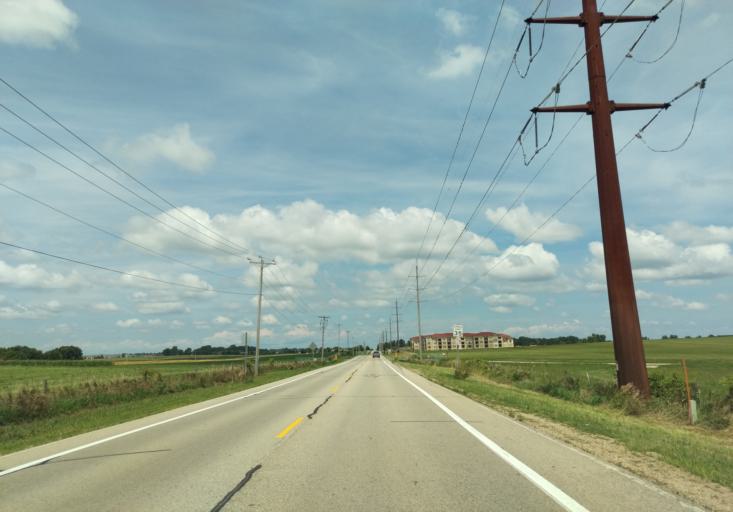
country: US
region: Wisconsin
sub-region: Dane County
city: Middleton
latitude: 43.0630
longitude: -89.5373
